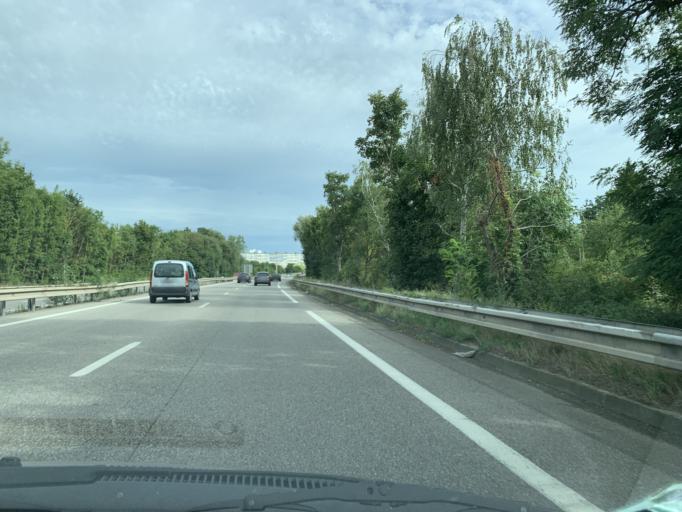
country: FR
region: Alsace
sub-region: Departement du Haut-Rhin
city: Morschwiller-le-Bas
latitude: 47.7409
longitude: 7.2849
